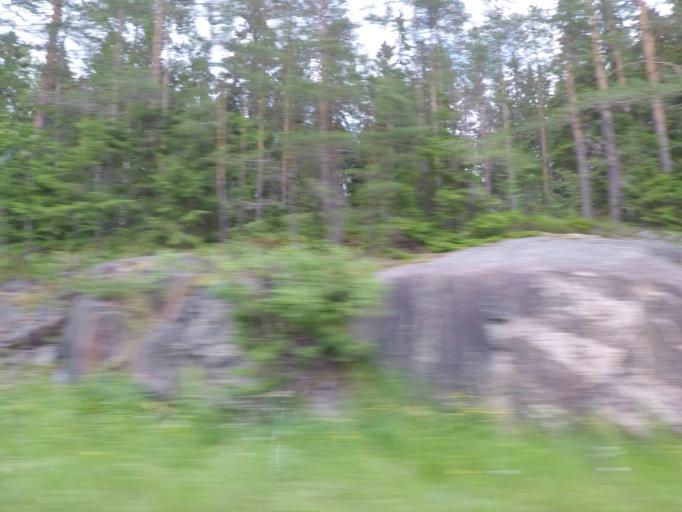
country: FI
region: Paijanne Tavastia
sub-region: Lahti
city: Hollola
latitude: 60.8439
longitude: 25.4947
